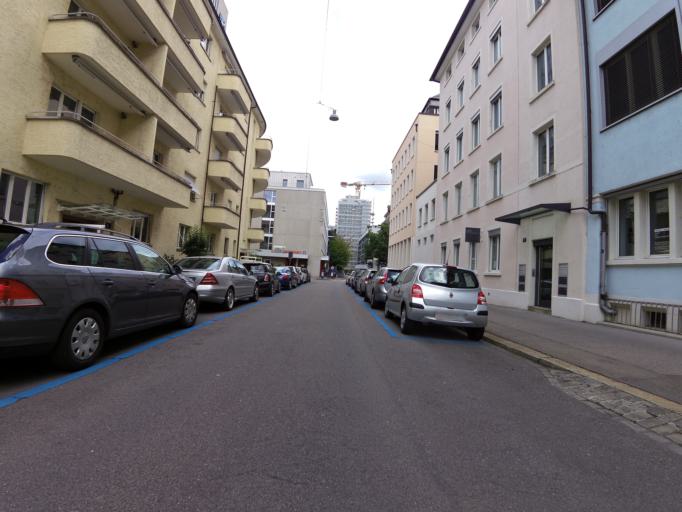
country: CH
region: Zurich
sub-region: Bezirk Zuerich
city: Zuerich (Kreis 4) / Werd
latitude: 47.3710
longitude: 8.5269
